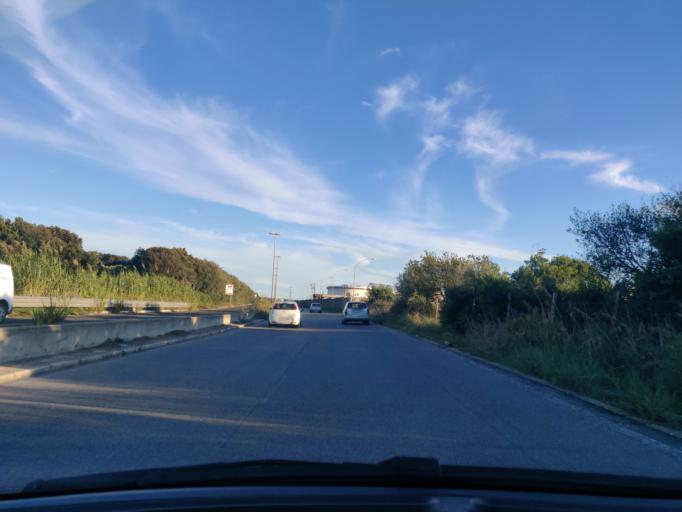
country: IT
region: Latium
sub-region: Citta metropolitana di Roma Capitale
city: Civitavecchia
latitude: 42.1137
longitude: 11.7801
